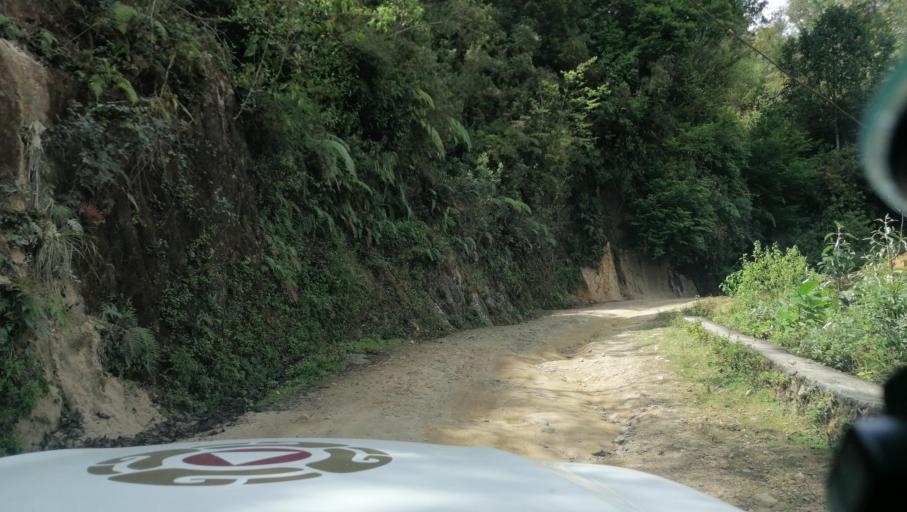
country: MX
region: Chiapas
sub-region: Cacahoatan
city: Benito Juarez
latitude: 15.1996
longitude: -92.2248
